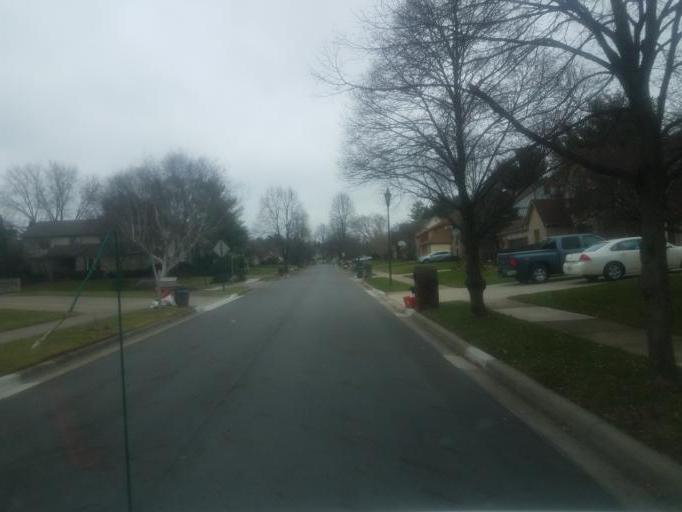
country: US
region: Ohio
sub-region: Franklin County
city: Westerville
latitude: 40.1298
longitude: -82.9534
